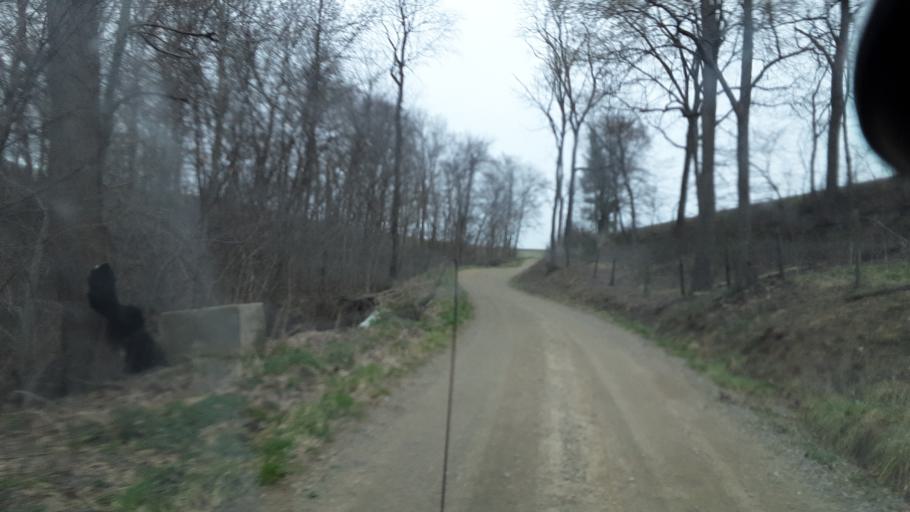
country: US
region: Ohio
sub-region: Coshocton County
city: West Lafayette
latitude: 40.3359
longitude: -81.6949
